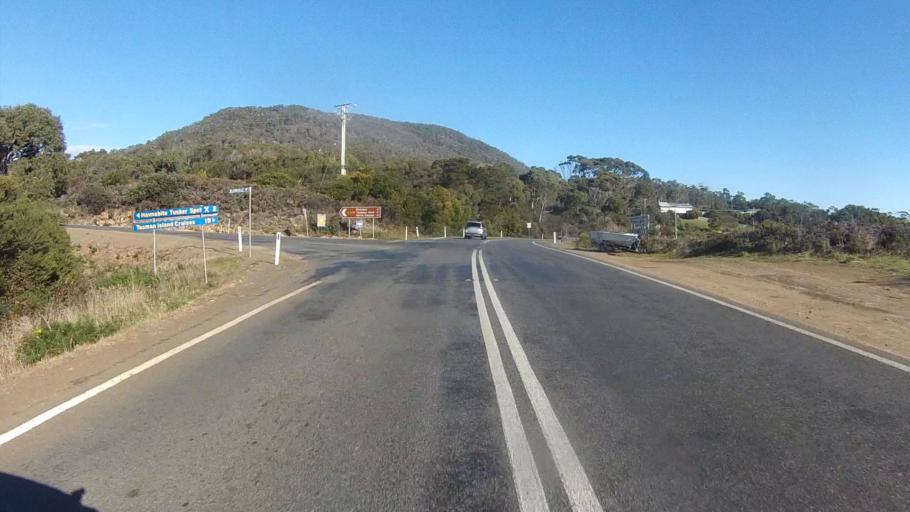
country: AU
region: Tasmania
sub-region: Sorell
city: Sorell
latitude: -43.0182
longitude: 147.9247
